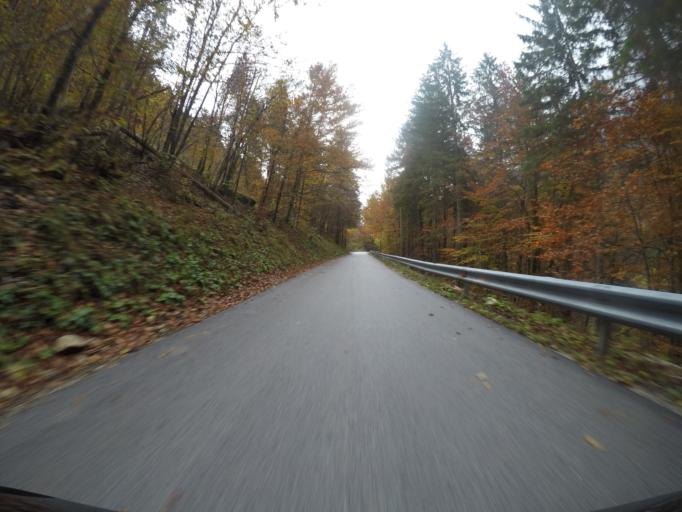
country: SI
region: Jesenice
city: Hrusica
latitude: 46.3965
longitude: 14.0041
